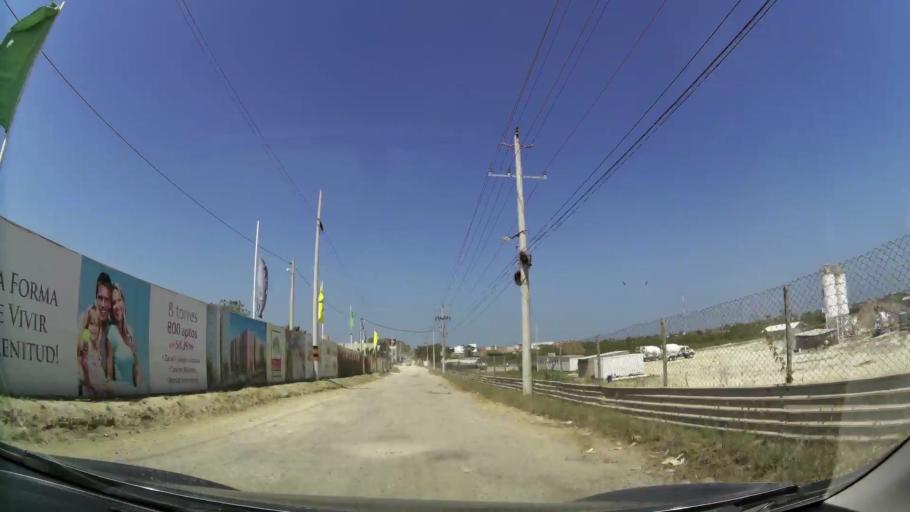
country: CO
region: Bolivar
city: Cartagena
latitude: 10.3988
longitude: -75.4551
